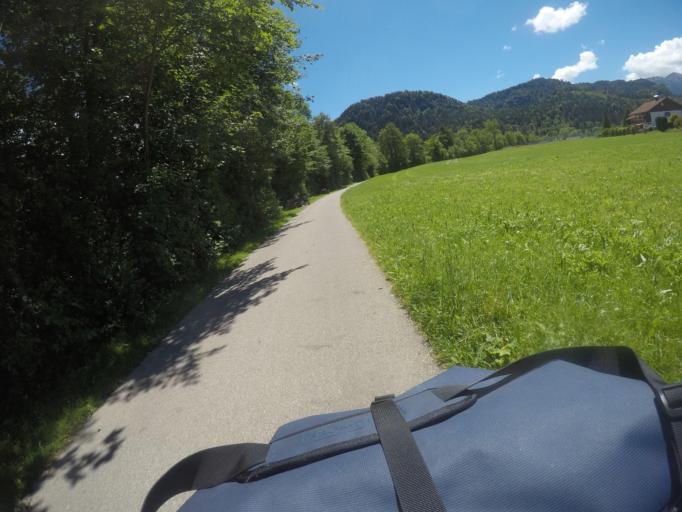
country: DE
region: Bavaria
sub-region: Swabia
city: Fuessen
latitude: 47.5706
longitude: 10.7118
